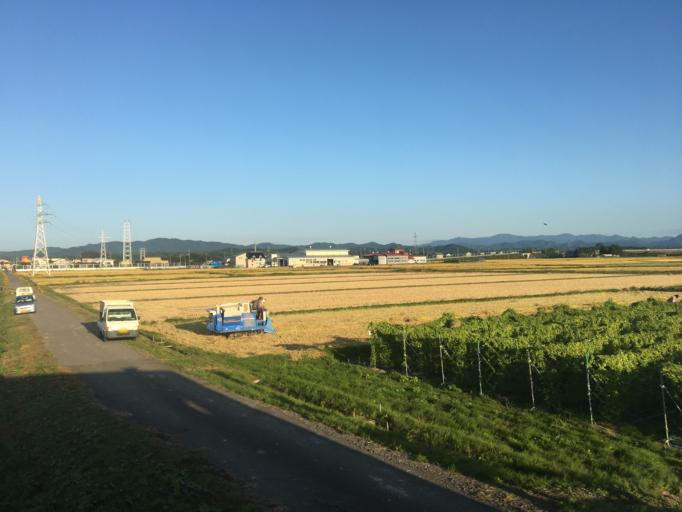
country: JP
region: Akita
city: Takanosu
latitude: 40.2213
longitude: 140.3562
